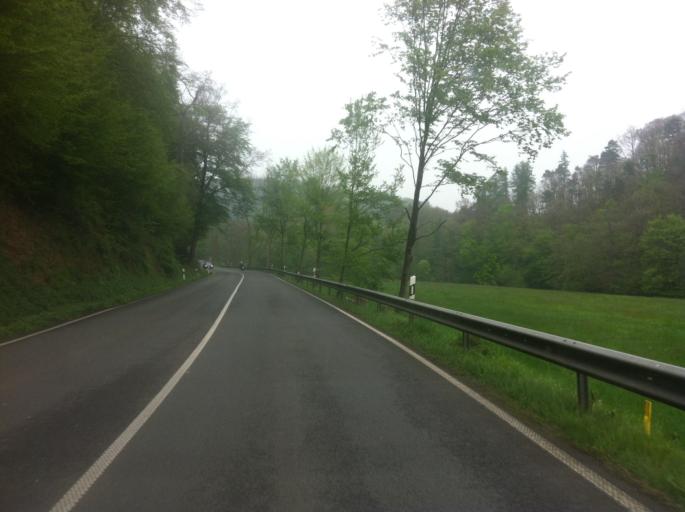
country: DE
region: North Rhine-Westphalia
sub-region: Regierungsbezirk Koln
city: Hennef
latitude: 50.7968
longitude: 7.3371
